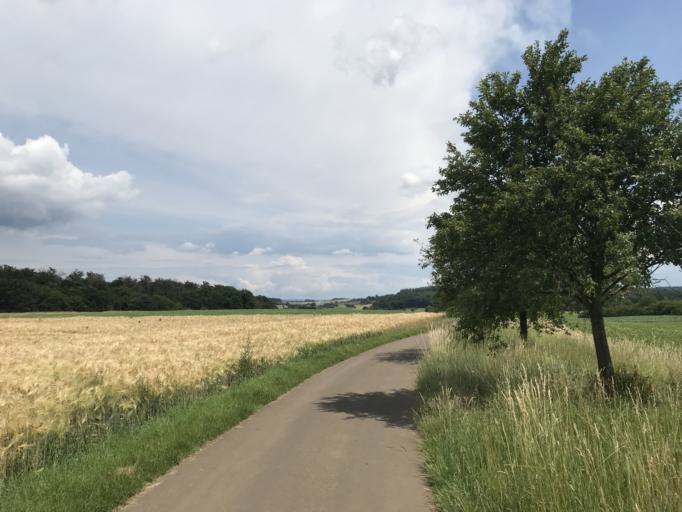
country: DE
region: Hesse
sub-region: Regierungsbezirk Giessen
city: Hungen
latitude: 50.4708
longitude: 8.9265
